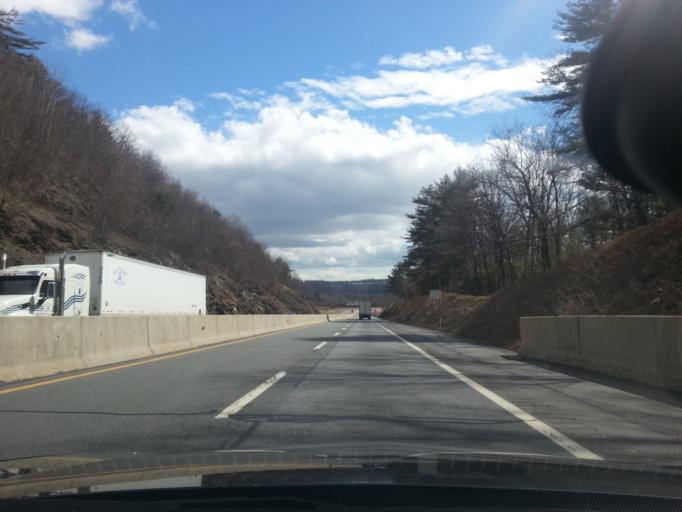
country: US
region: Pennsylvania
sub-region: Carbon County
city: Weissport East
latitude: 40.8654
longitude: -75.6522
